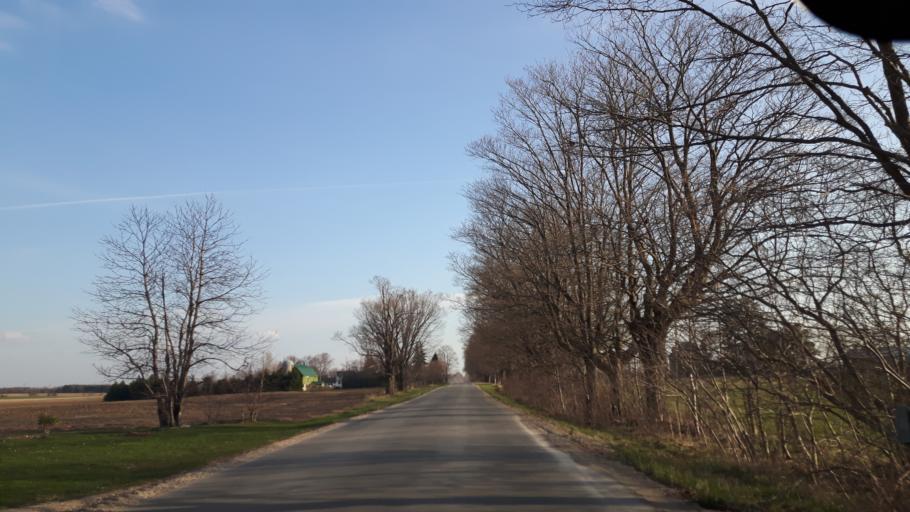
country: CA
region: Ontario
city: Goderich
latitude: 43.6418
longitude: -81.6643
